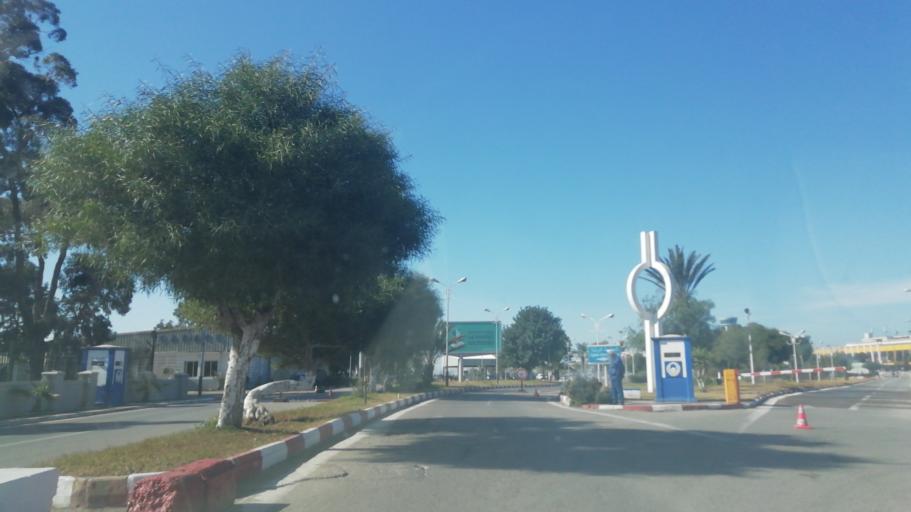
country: DZ
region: Oran
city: Es Senia
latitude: 35.6195
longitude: -0.6022
